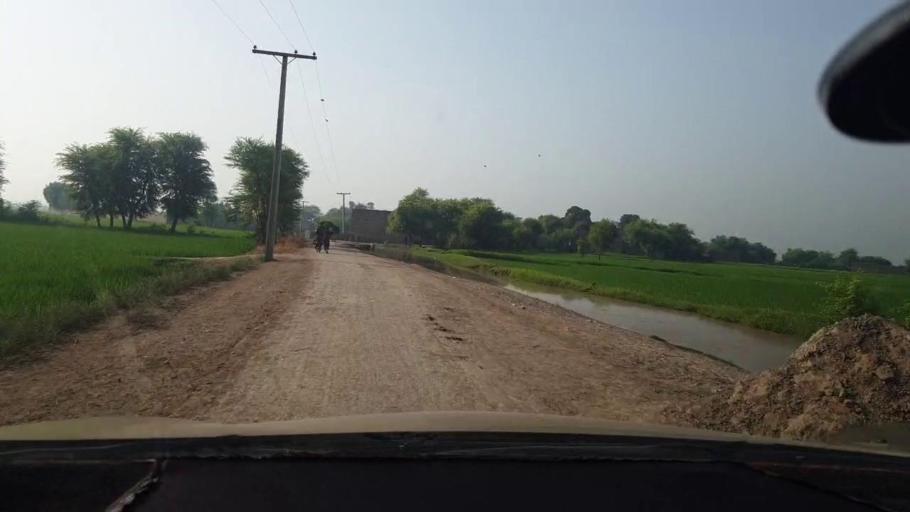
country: PK
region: Sindh
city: Kambar
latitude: 27.5364
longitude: 68.0187
